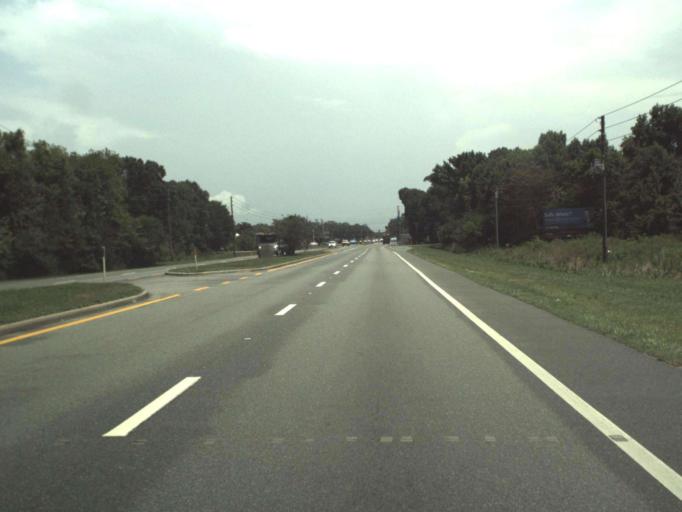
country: US
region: Florida
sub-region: Sumter County
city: Wildwood
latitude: 28.8423
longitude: -82.0454
